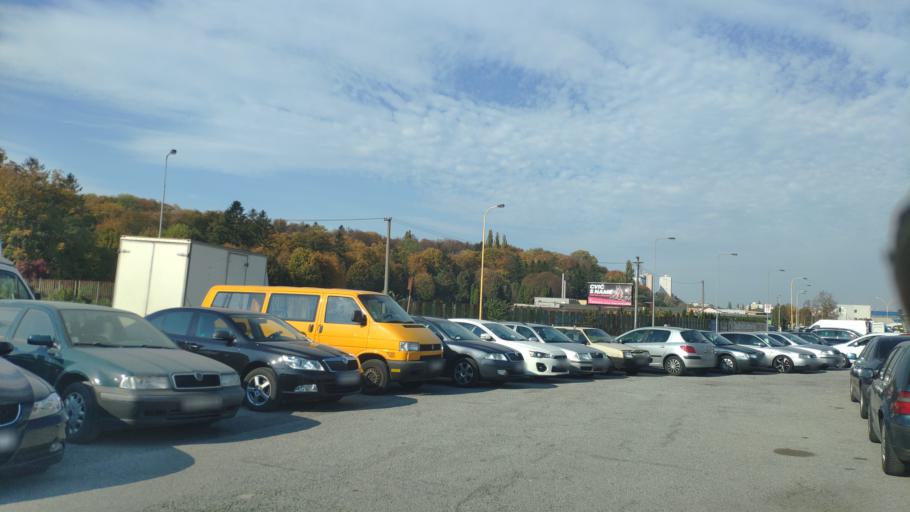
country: SK
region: Kosicky
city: Kosice
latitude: 48.6924
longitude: 21.2620
